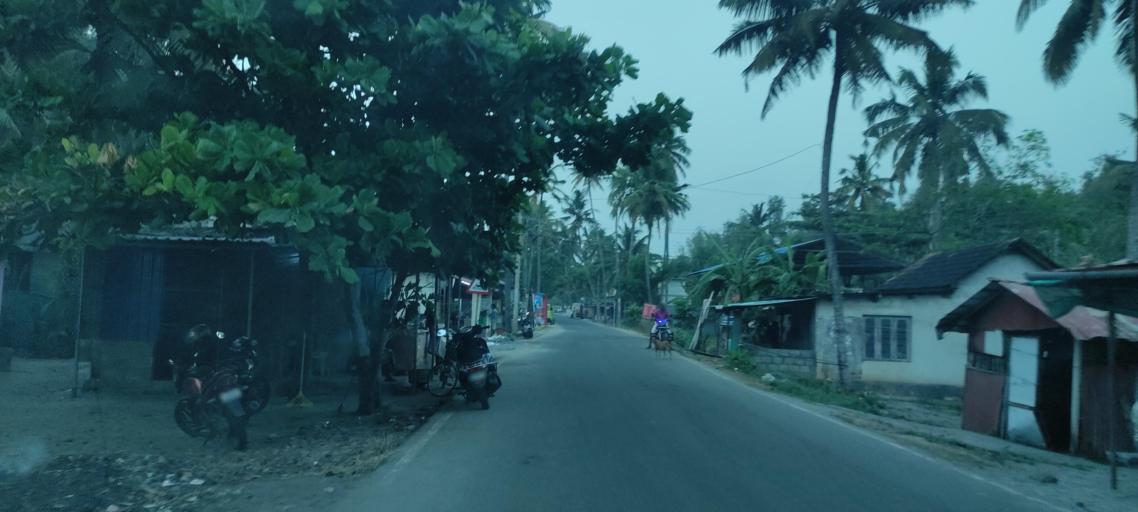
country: IN
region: Kerala
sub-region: Alappuzha
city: Kayankulam
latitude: 9.1309
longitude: 76.4655
